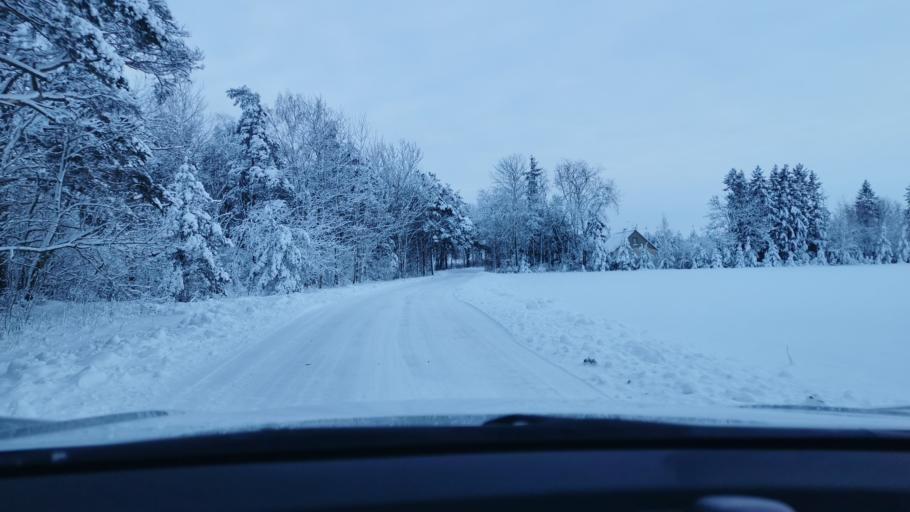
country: EE
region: Laeaene-Virumaa
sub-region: Haljala vald
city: Haljala
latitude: 59.5051
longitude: 26.2914
